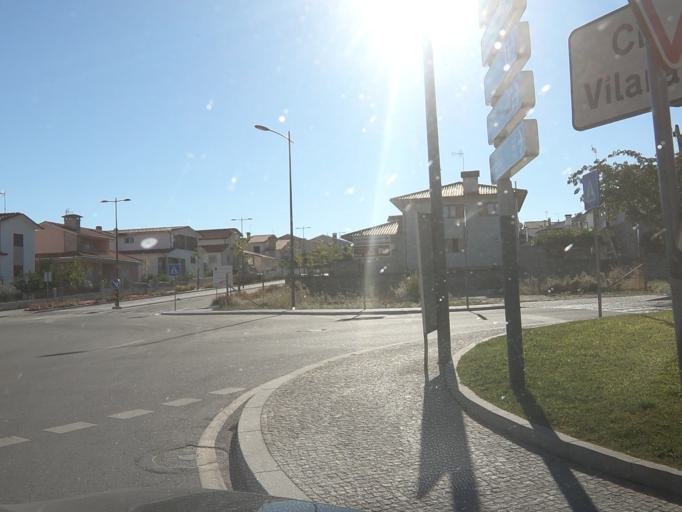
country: PT
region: Vila Real
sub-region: Valpacos
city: Valpacos
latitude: 41.6067
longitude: -7.3135
